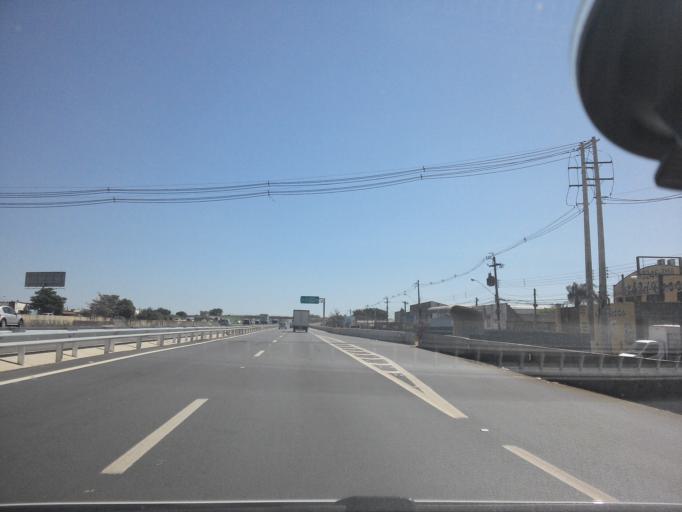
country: BR
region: Sao Paulo
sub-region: Campinas
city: Campinas
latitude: -22.8501
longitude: -47.1078
